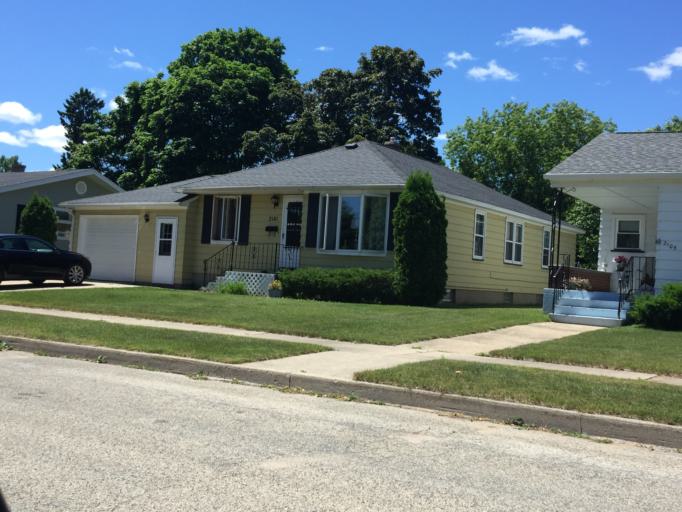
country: US
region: Michigan
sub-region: Menominee County
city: Menominee
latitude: 45.1183
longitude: -87.6196
